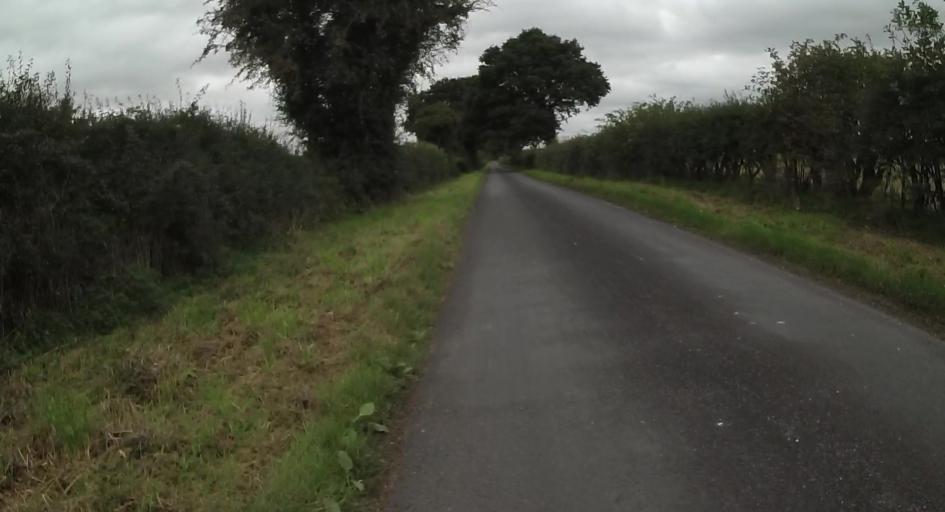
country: GB
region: England
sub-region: Hampshire
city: Four Marks
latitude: 51.1560
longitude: -1.1173
